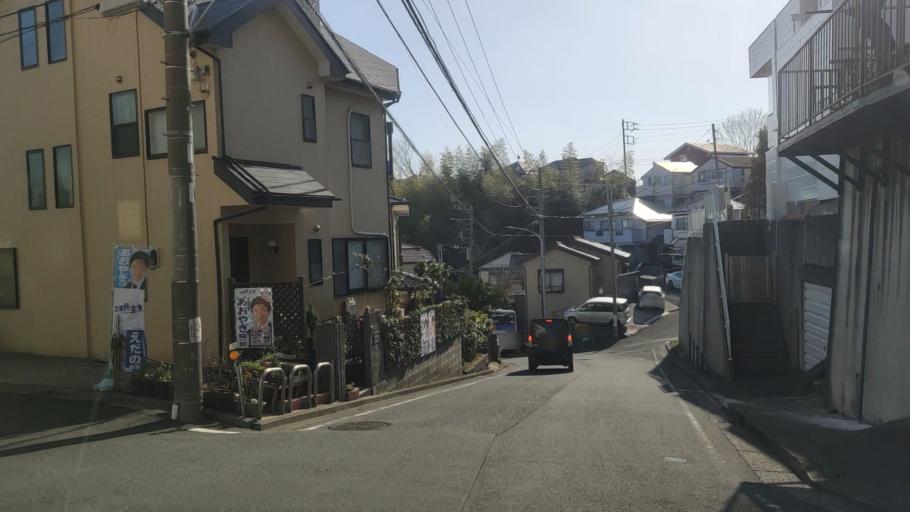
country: JP
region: Kanagawa
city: Yokohama
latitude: 35.4609
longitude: 139.6027
